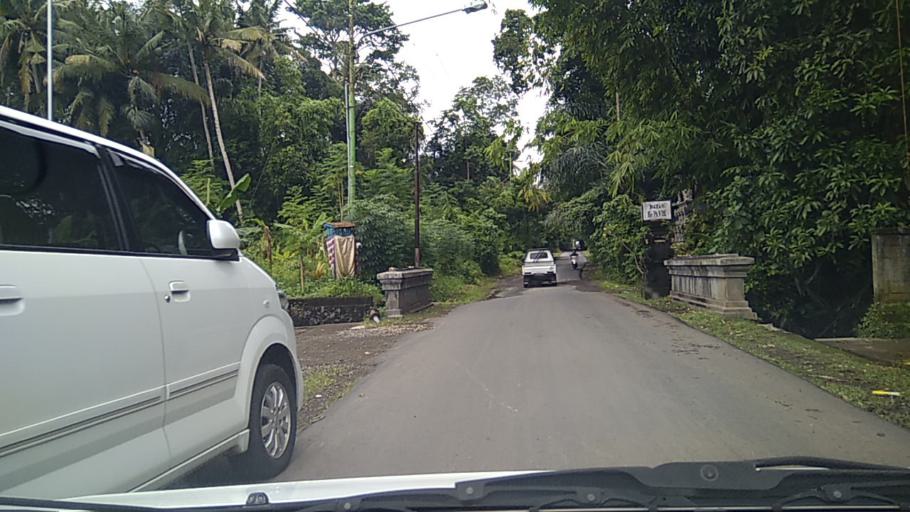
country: ID
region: Bali
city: Banjar Keraman
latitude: -8.5223
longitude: 115.2155
